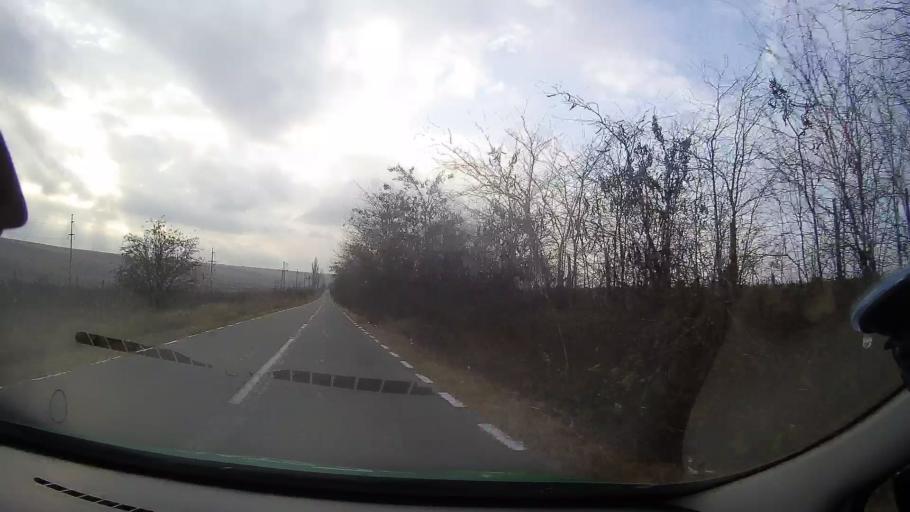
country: RO
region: Constanta
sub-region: Comuna Mircea Voda
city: Satu Nou
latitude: 44.2377
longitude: 28.2465
